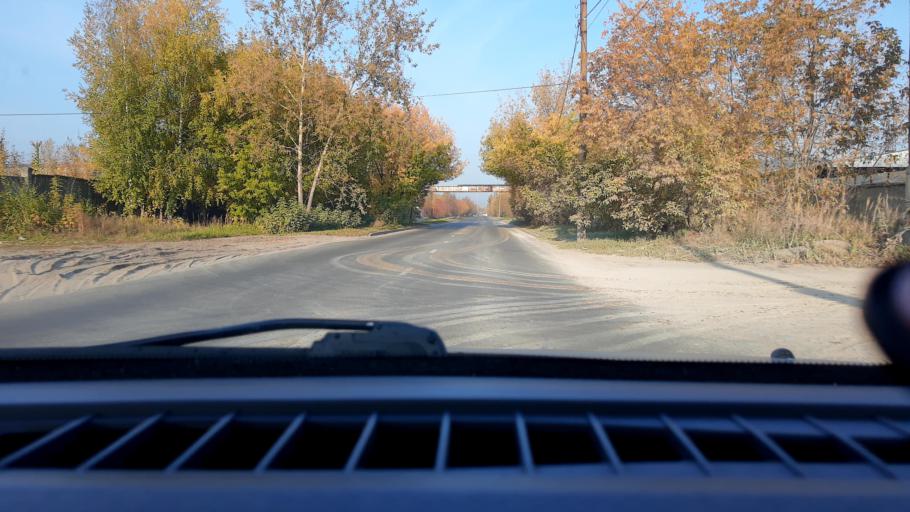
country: RU
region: Nizjnij Novgorod
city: Gorbatovka
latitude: 56.3489
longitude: 43.8127
